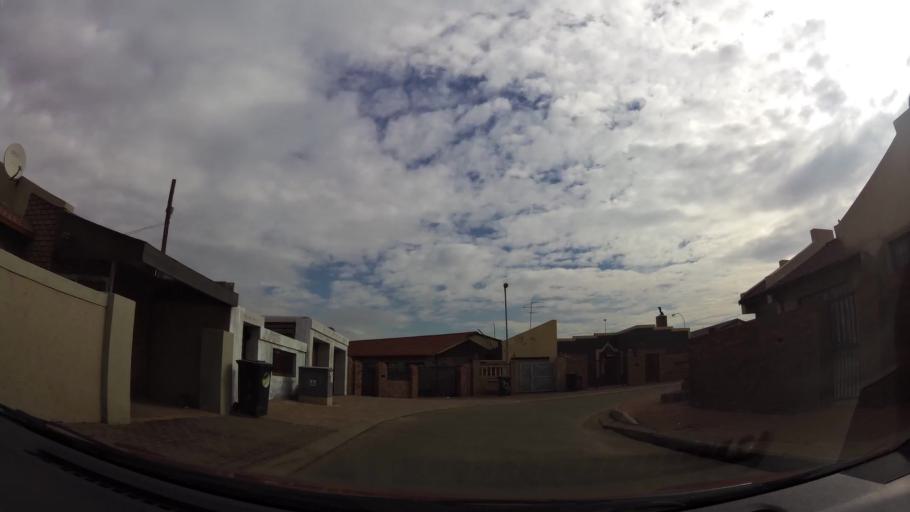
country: ZA
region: Gauteng
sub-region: City of Johannesburg Metropolitan Municipality
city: Soweto
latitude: -26.2742
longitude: 27.8290
